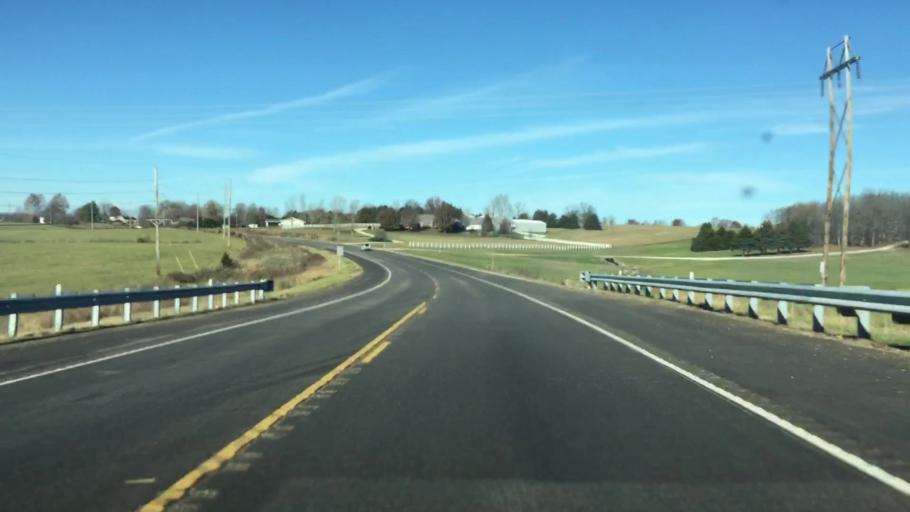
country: US
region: Missouri
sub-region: Miller County
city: Eldon
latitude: 38.3712
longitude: -92.6180
